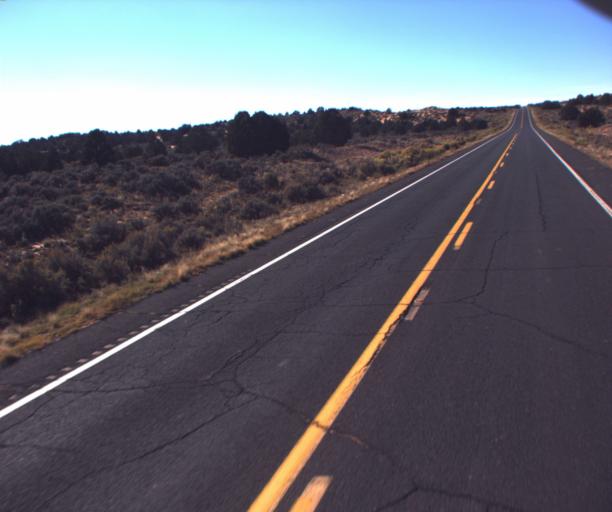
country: US
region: Arizona
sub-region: Coconino County
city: Kaibito
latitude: 36.5785
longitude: -110.7831
